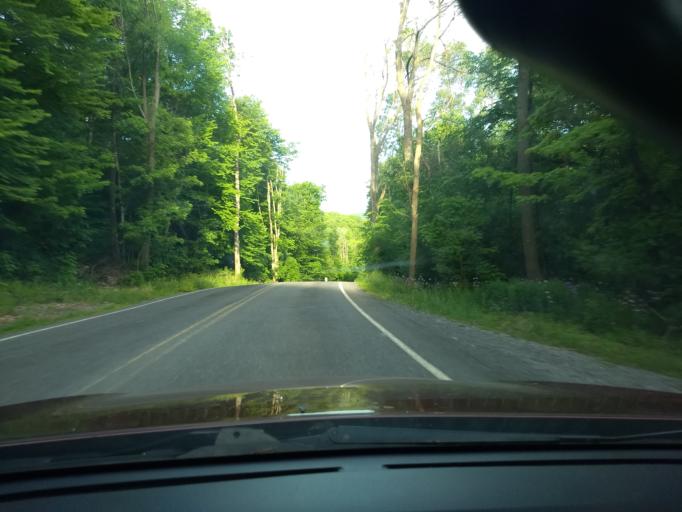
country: US
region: Pennsylvania
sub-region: Cambria County
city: Gallitzin
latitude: 40.5032
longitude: -78.5176
